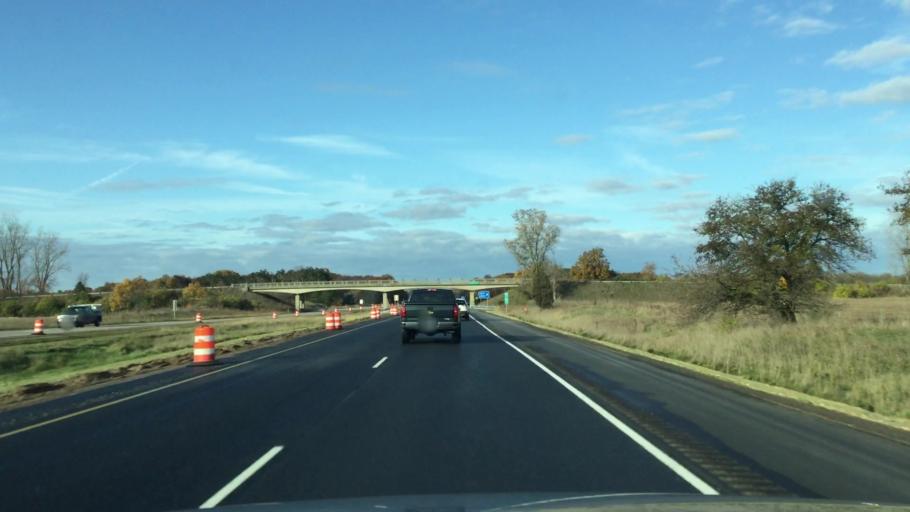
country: US
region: Michigan
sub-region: Calhoun County
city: Marshall
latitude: 42.2829
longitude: -84.9042
